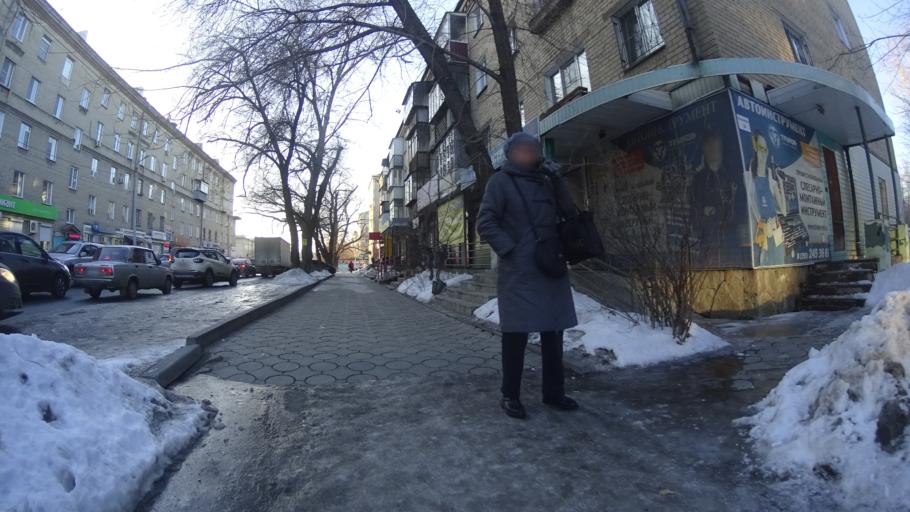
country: RU
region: Chelyabinsk
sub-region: Gorod Chelyabinsk
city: Chelyabinsk
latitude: 55.1389
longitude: 61.4426
